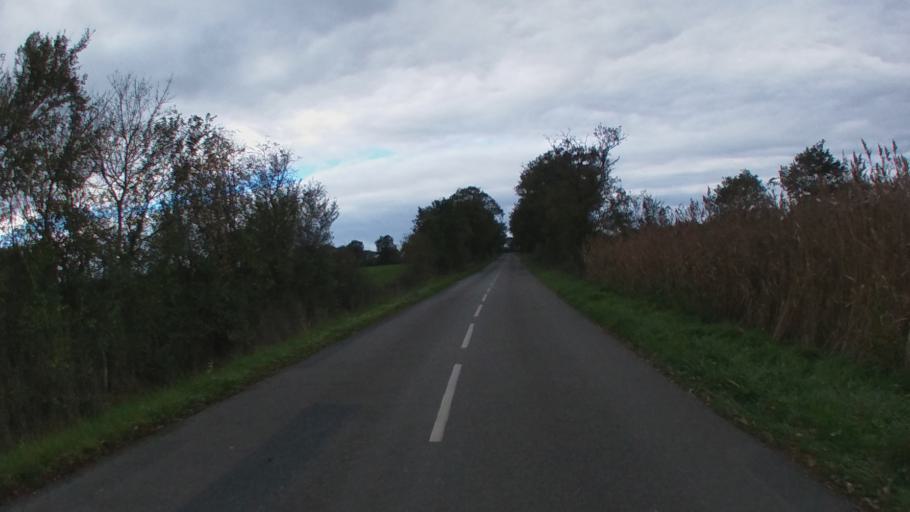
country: FR
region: Pays de la Loire
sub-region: Departement de la Loire-Atlantique
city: Corsept
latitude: 47.2647
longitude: -2.0928
